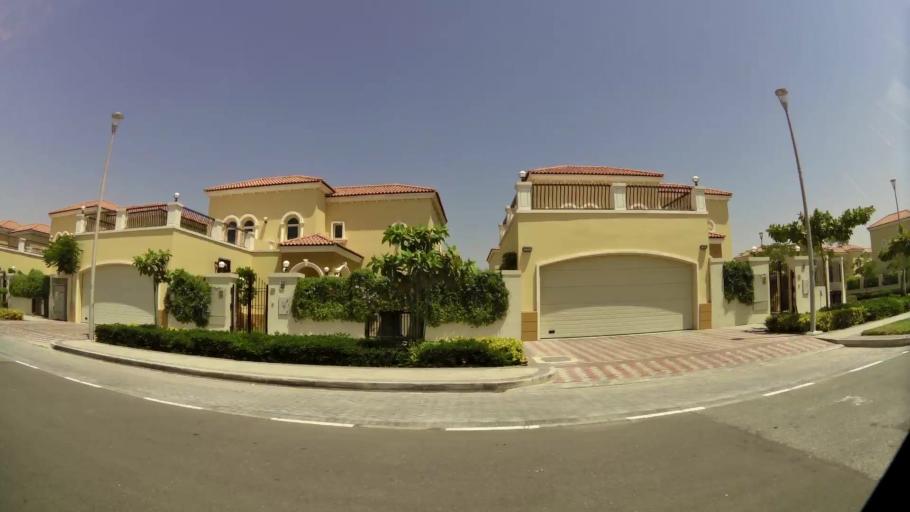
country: AE
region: Dubai
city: Dubai
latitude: 25.0379
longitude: 55.1686
